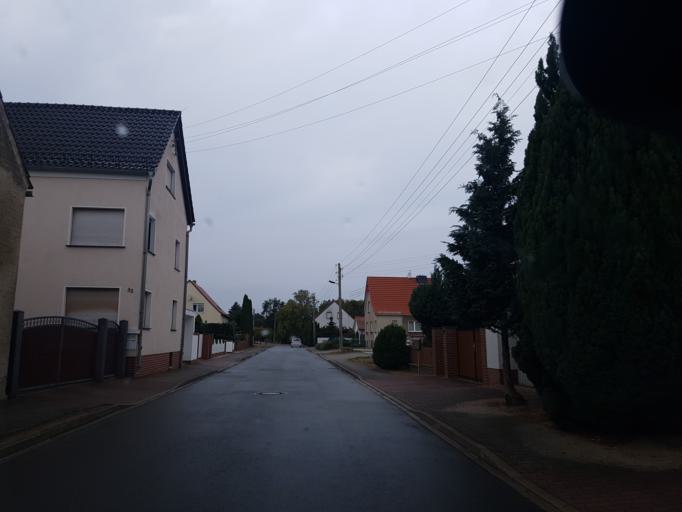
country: DE
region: Saxony-Anhalt
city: Jessen
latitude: 51.7690
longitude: 12.9000
